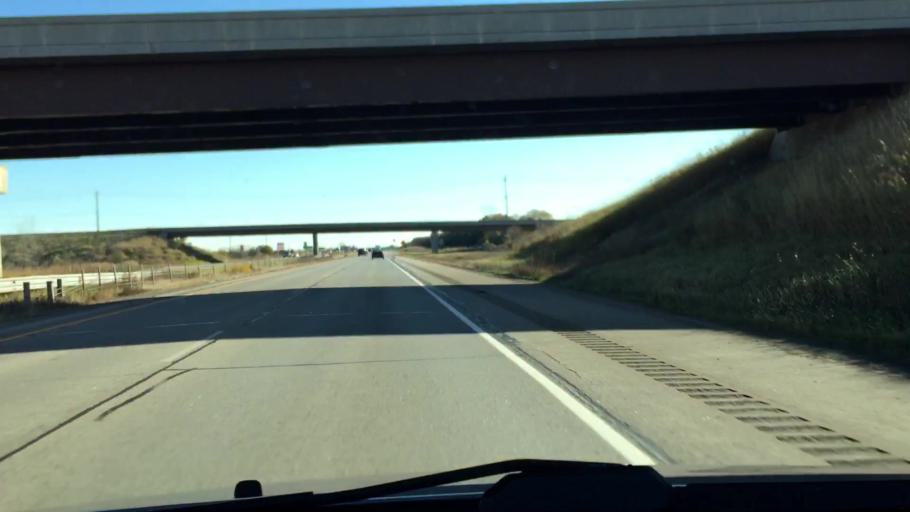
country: US
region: Wisconsin
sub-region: Outagamie County
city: Kimberly
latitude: 44.2979
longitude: -88.3560
